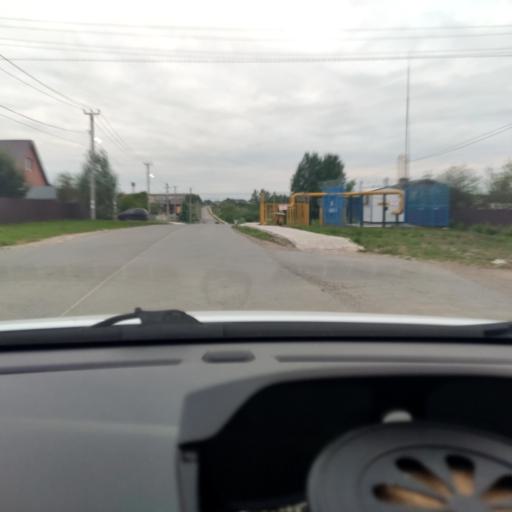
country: RU
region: Tatarstan
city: Vysokaya Gora
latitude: 55.9131
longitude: 49.3304
